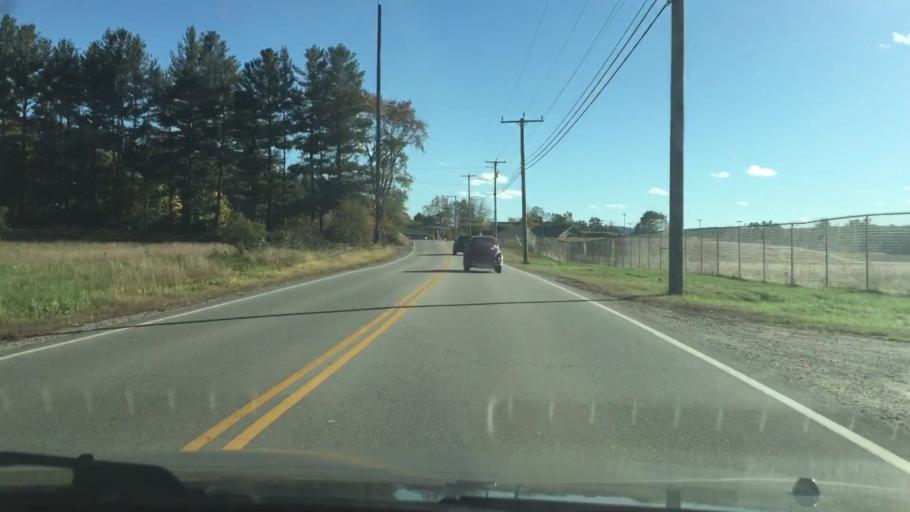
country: US
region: New Hampshire
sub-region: Cheshire County
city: Swanzey
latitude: 42.8816
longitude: -72.2701
